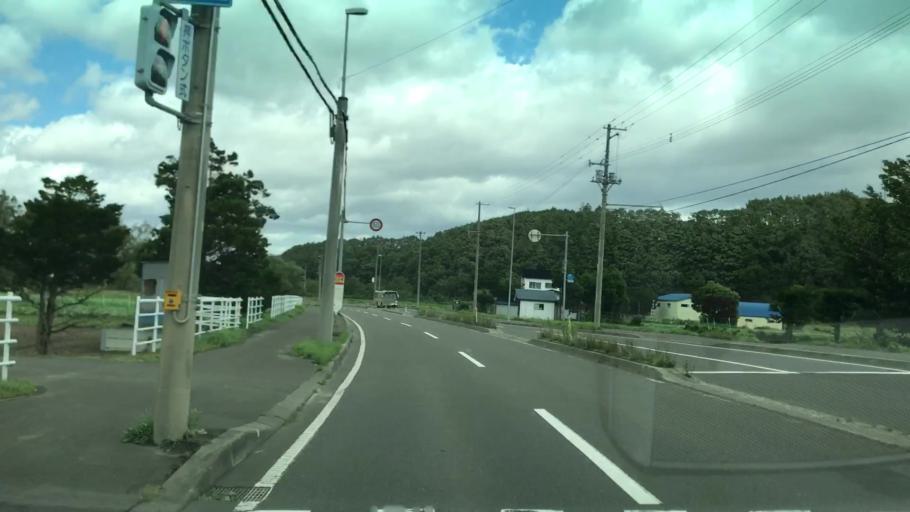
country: JP
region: Hokkaido
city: Kitahiroshima
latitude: 42.9749
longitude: 141.4490
